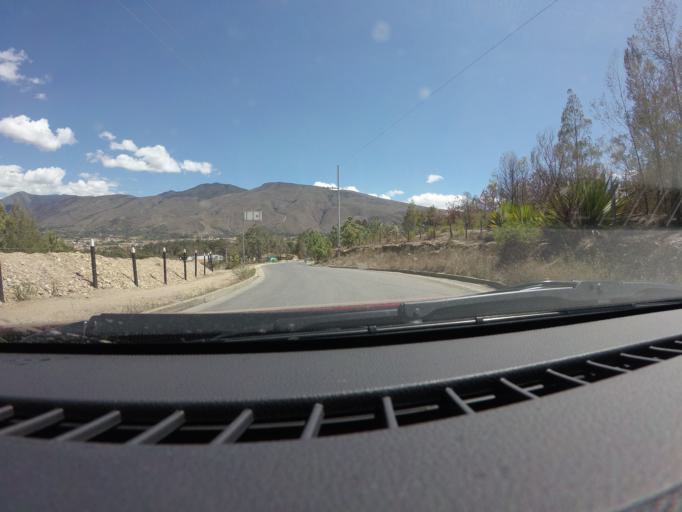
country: CO
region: Boyaca
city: Villa de Leiva
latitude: 5.6286
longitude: -73.5414
